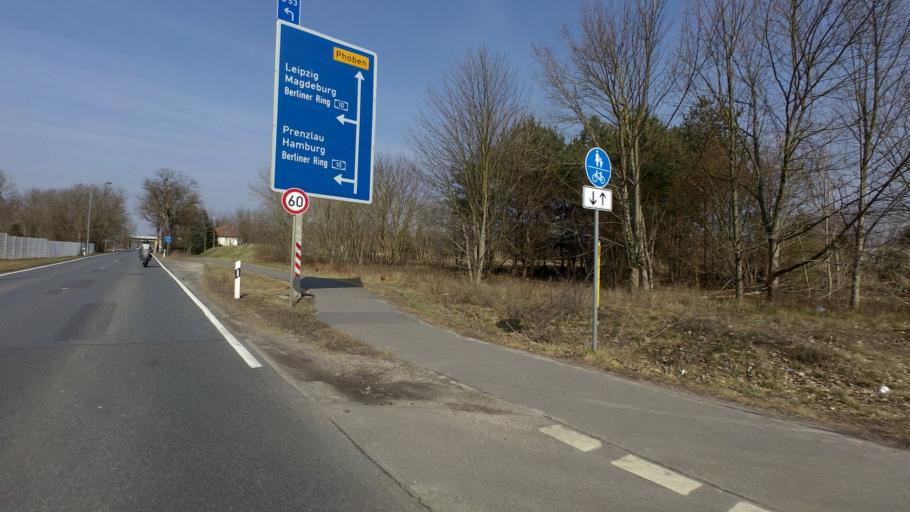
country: DE
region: Brandenburg
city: Werder
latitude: 52.4103
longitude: 12.9045
